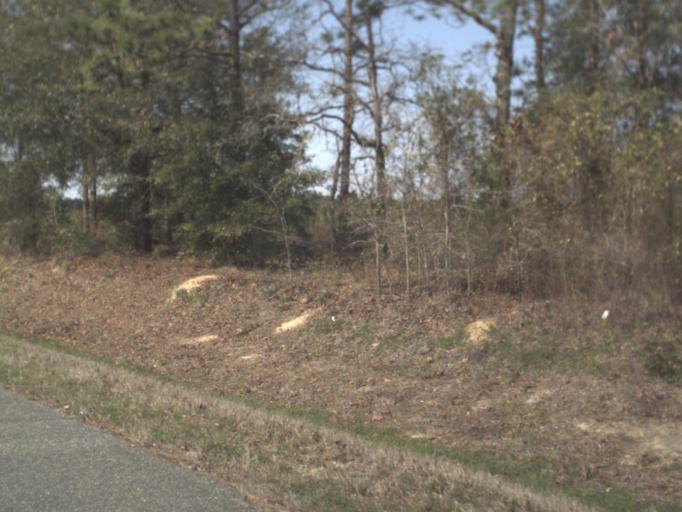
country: US
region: Florida
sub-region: Gadsden County
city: Gretna
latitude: 30.5289
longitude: -84.7863
